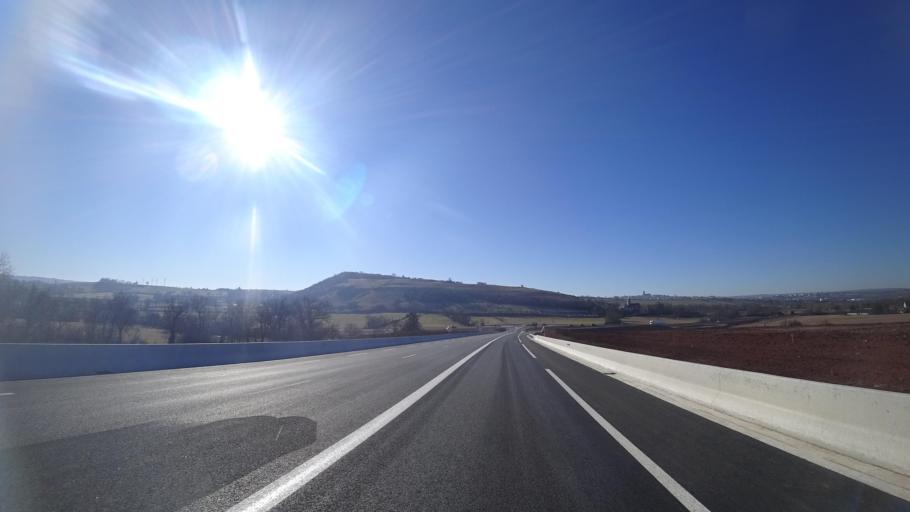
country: FR
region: Midi-Pyrenees
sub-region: Departement de l'Aveyron
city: Sebazac-Concoures
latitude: 44.3776
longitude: 2.6145
